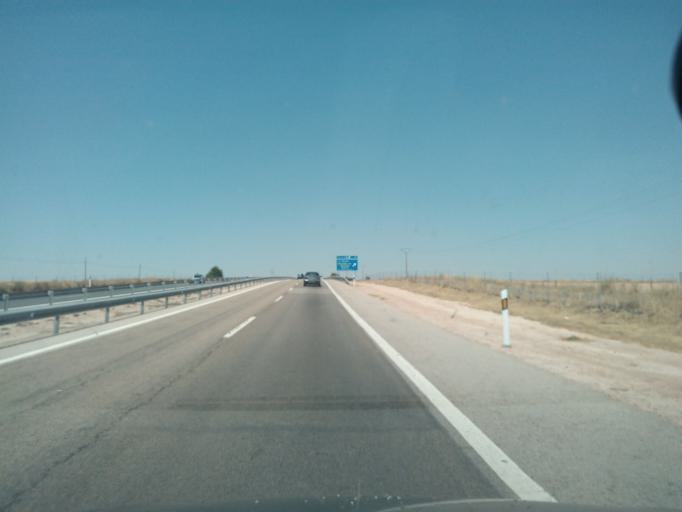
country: ES
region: Castille-La Mancha
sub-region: Province of Toledo
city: Tembleque
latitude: 39.7525
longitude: -3.4842
